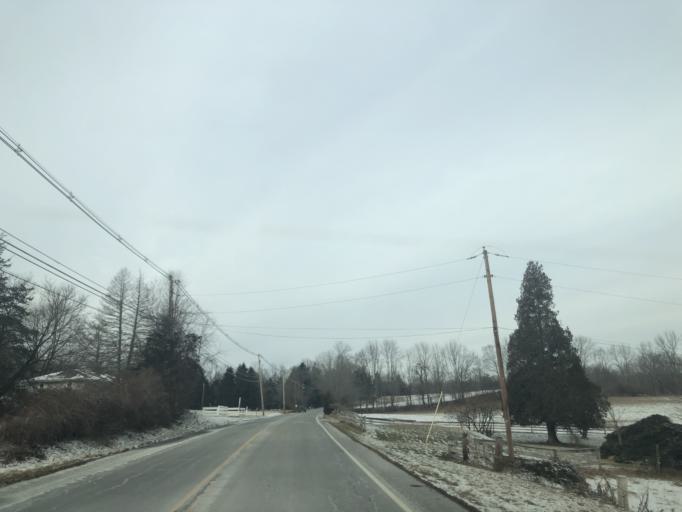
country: US
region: New Jersey
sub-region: Warren County
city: Oxford
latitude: 40.9216
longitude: -74.9898
